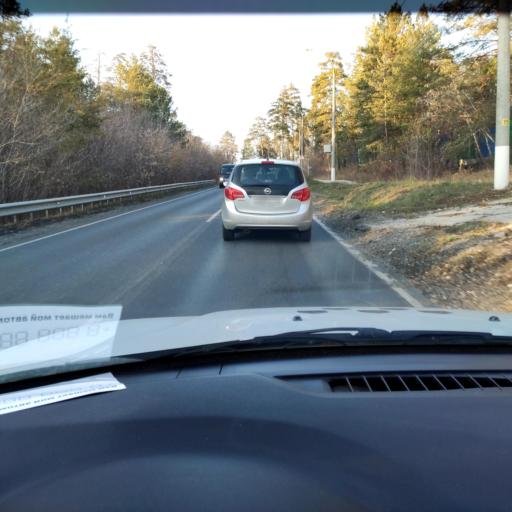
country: RU
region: Samara
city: Tol'yatti
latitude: 53.4794
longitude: 49.3227
